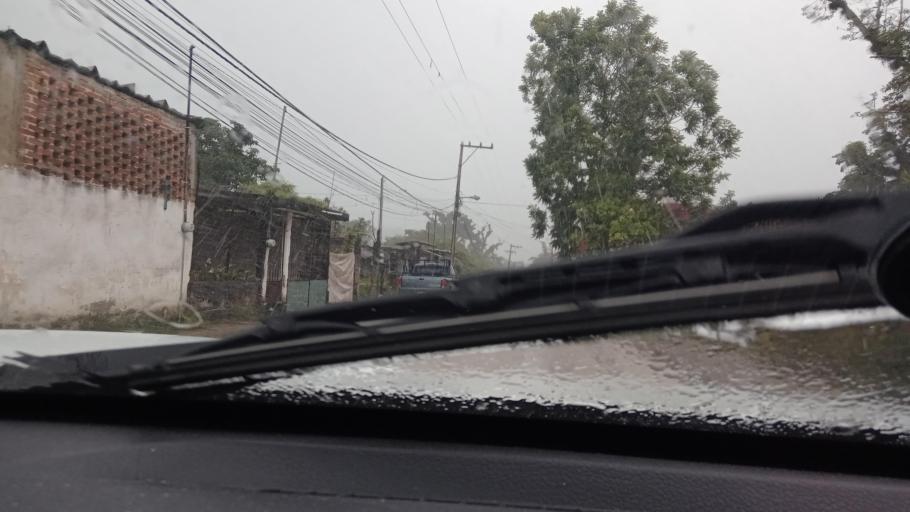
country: MX
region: Veracruz
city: Coatepec
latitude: 19.4592
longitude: -96.9757
